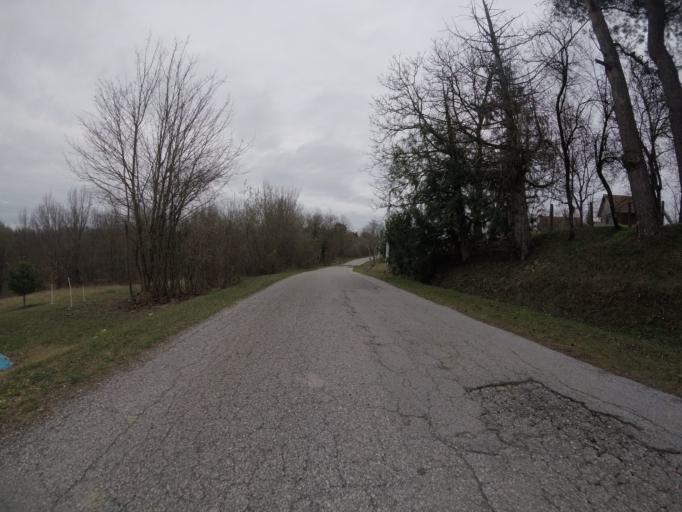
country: HR
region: Zagrebacka
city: Lukavec
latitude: 45.5685
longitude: 15.9718
